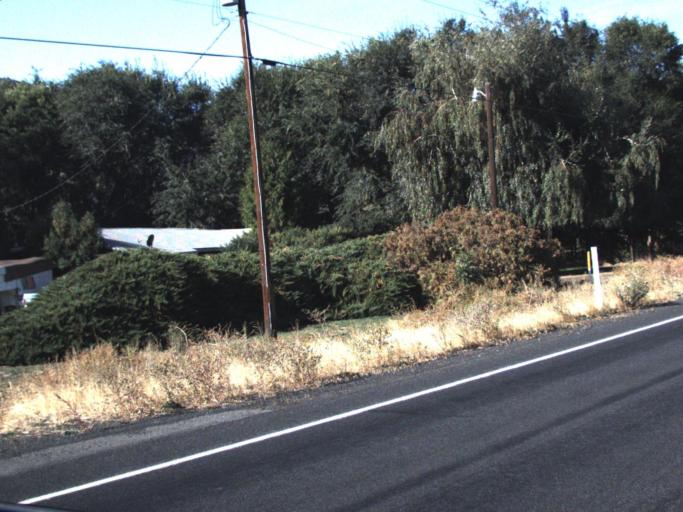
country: US
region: Washington
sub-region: Yakima County
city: Tieton
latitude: 46.7344
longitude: -120.7224
